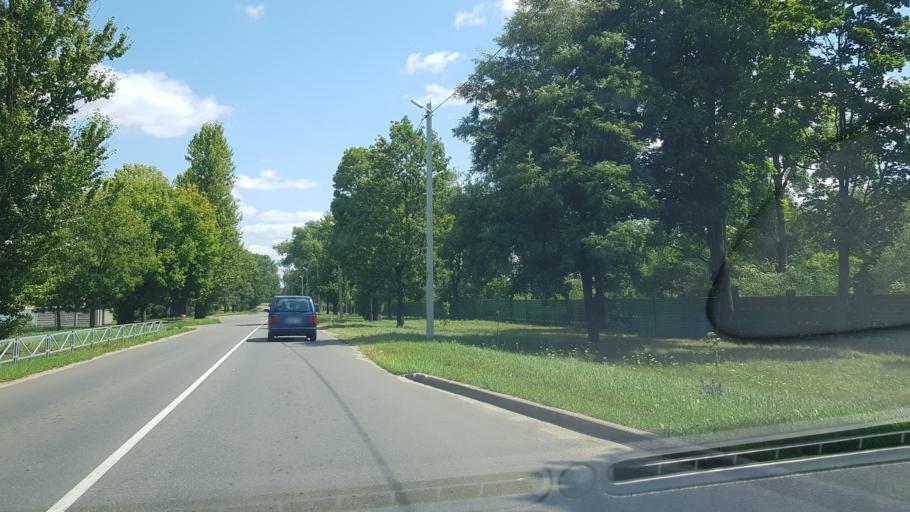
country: BY
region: Mogilev
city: Babruysk
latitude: 53.1078
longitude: 29.1929
